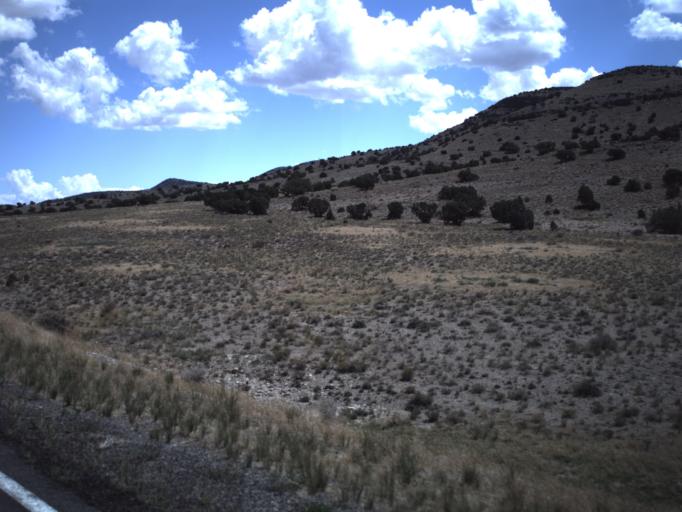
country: US
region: Utah
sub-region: Beaver County
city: Milford
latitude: 39.0735
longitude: -113.6414
